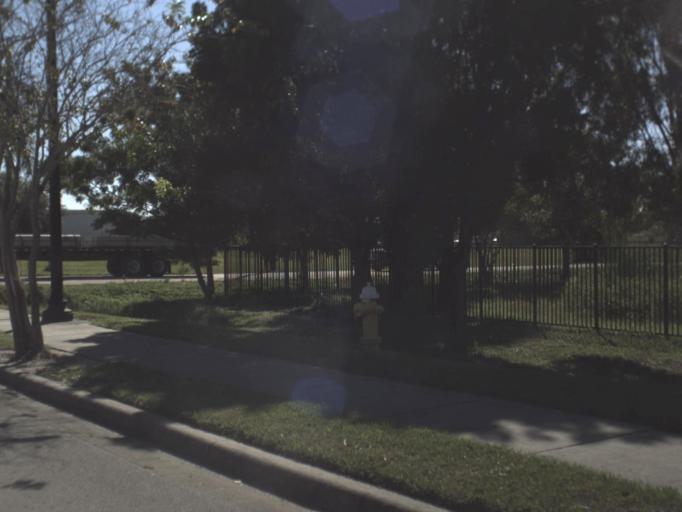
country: US
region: Florida
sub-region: Lee County
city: Fort Myers
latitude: 26.6412
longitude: -81.8332
